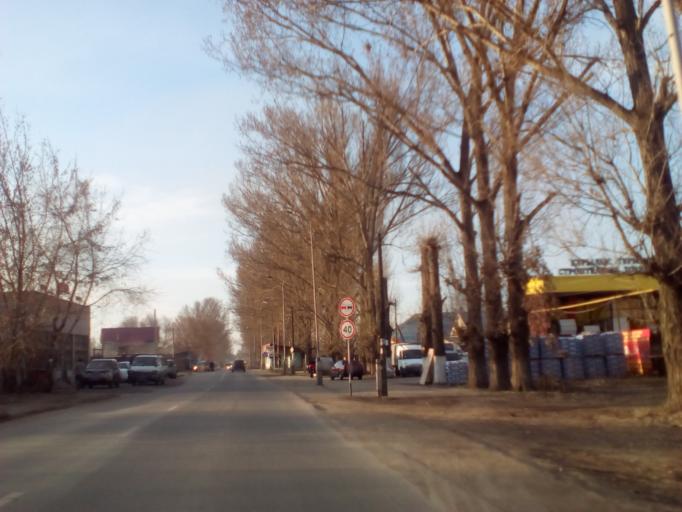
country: KZ
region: Almaty Oblysy
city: Burunday
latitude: 43.2534
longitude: 76.7828
